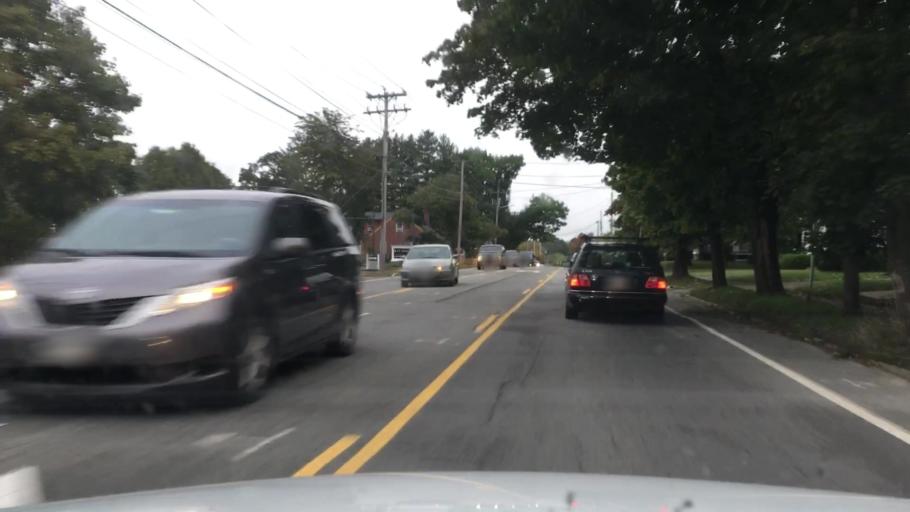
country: US
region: Maine
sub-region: Cumberland County
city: South Portland Gardens
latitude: 43.6699
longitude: -70.3046
